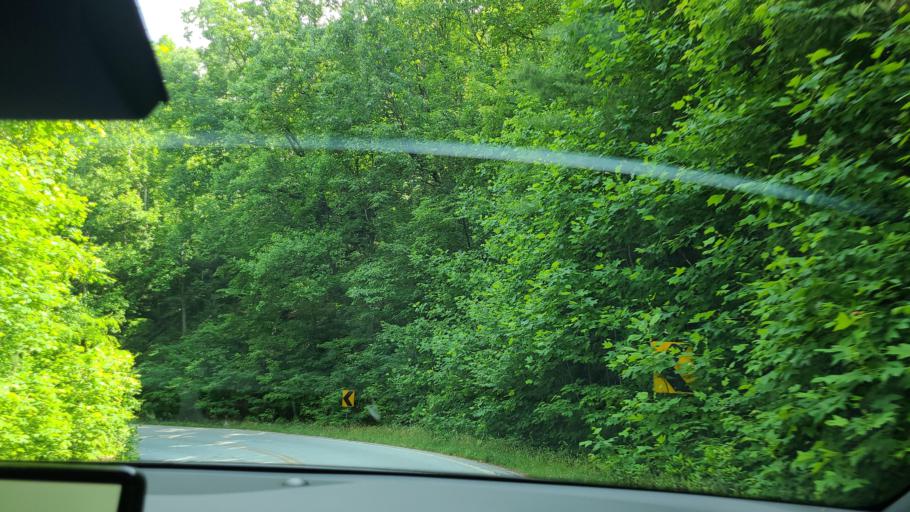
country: US
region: Georgia
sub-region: Rabun County
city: Mountain City
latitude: 35.0222
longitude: -83.1866
